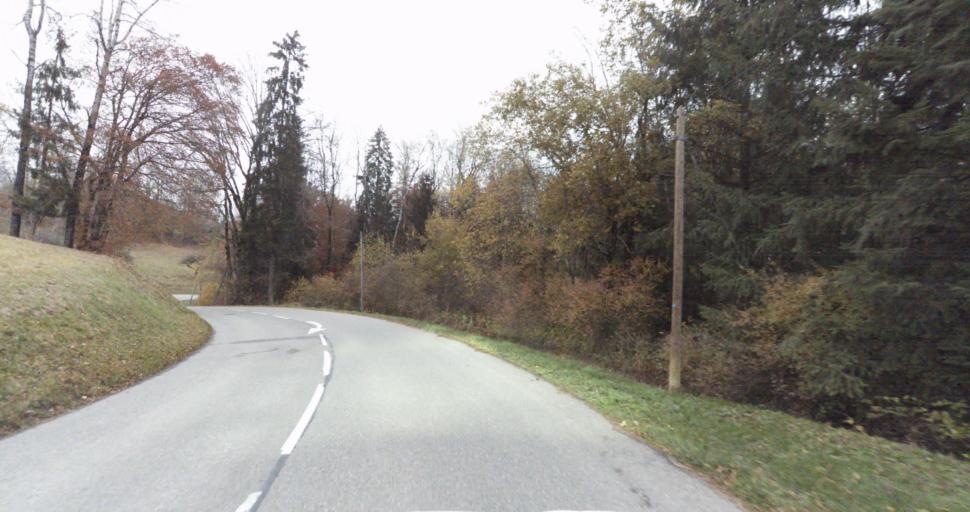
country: FR
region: Rhone-Alpes
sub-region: Departement de la Haute-Savoie
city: Saint-Jorioz
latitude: 45.7738
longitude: 6.1330
